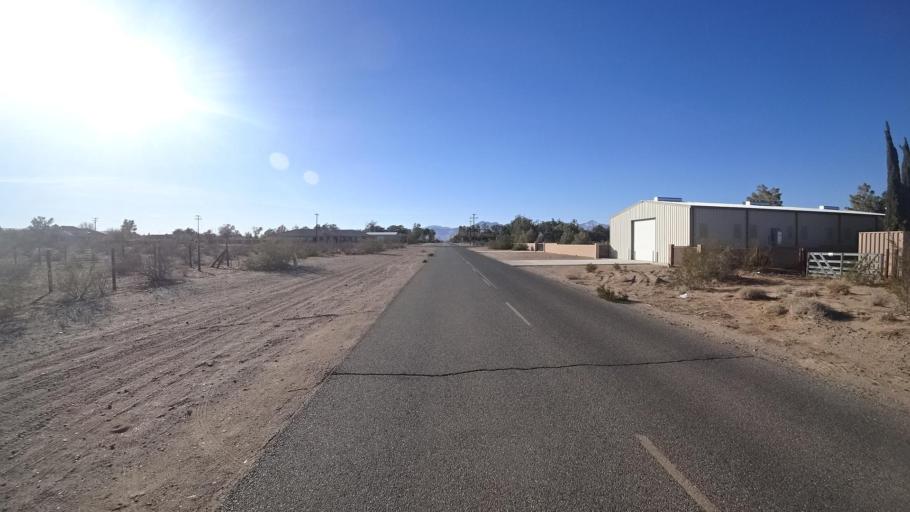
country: US
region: California
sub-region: Kern County
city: Ridgecrest
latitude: 35.6371
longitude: -117.7042
